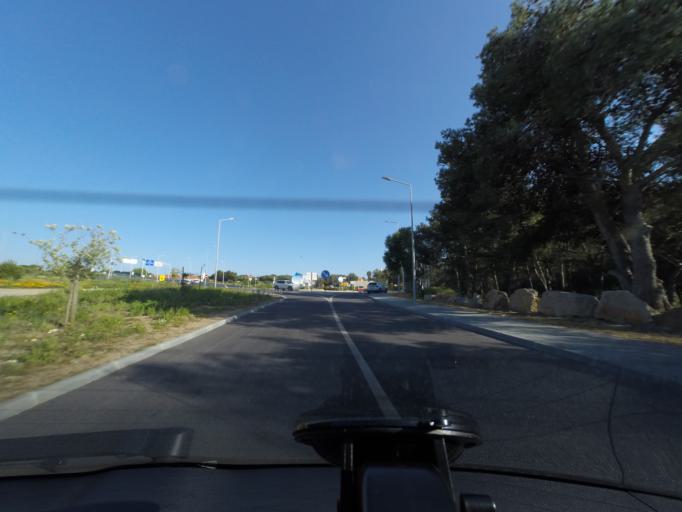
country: PT
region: Lisbon
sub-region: Cascais
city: Cascais
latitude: 38.7228
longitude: -9.4472
